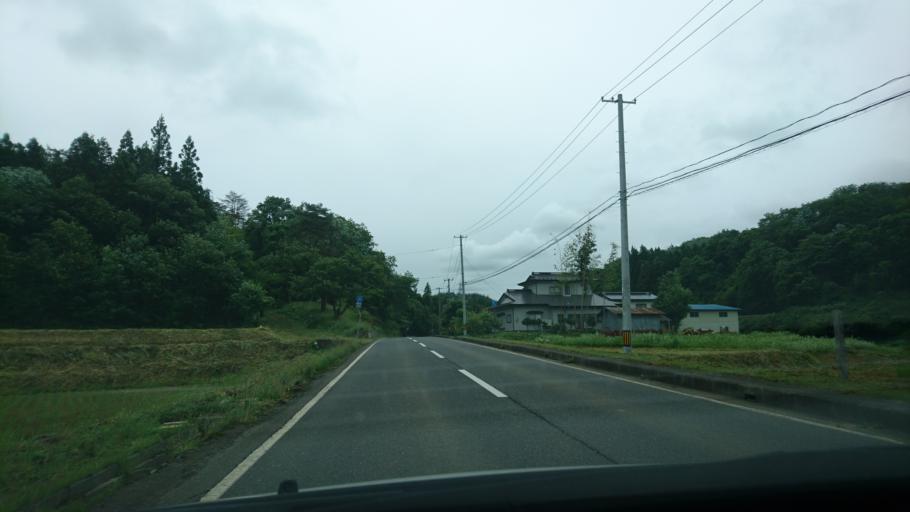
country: JP
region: Iwate
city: Ichinoseki
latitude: 38.9659
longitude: 141.0581
